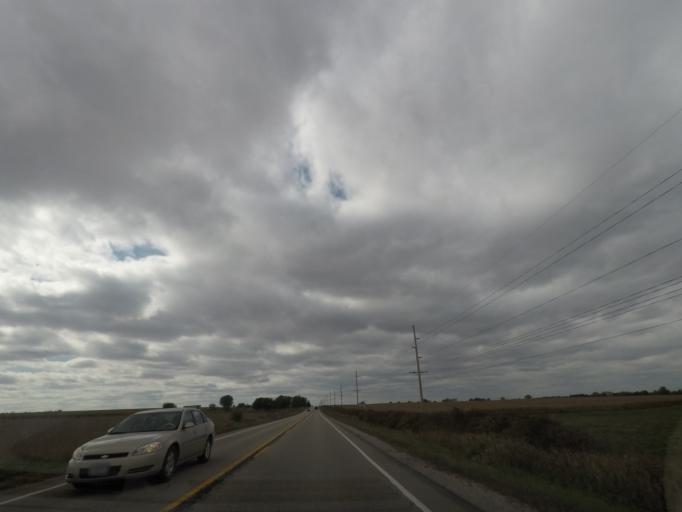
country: US
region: Iowa
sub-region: Story County
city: Huxley
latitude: 41.8778
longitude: -93.5428
